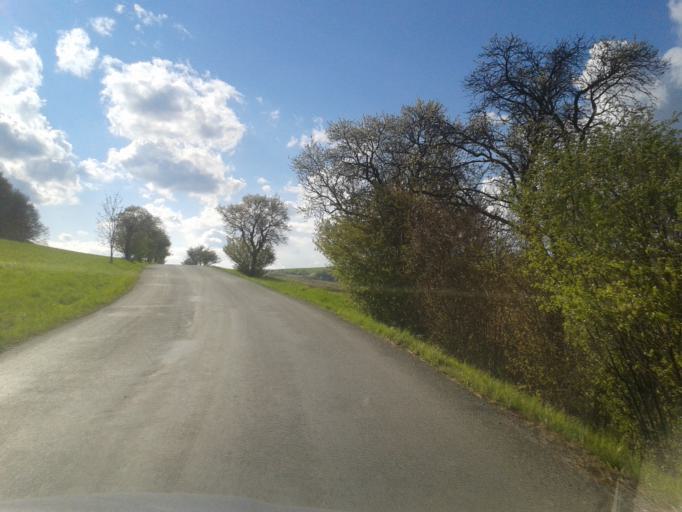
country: CZ
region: Central Bohemia
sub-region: Okres Beroun
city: Lodenice
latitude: 50.0097
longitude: 14.1311
